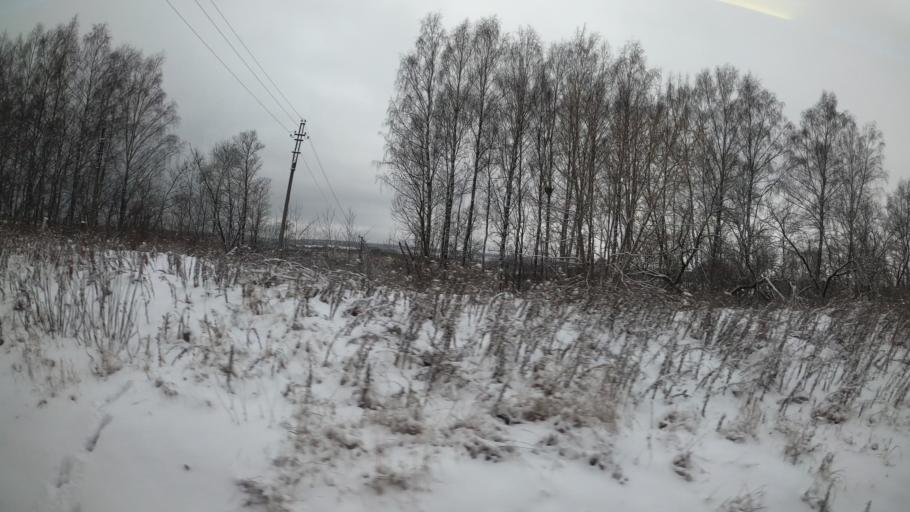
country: RU
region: Jaroslavl
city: Pereslavl'-Zalesskiy
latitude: 56.6810
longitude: 38.9192
